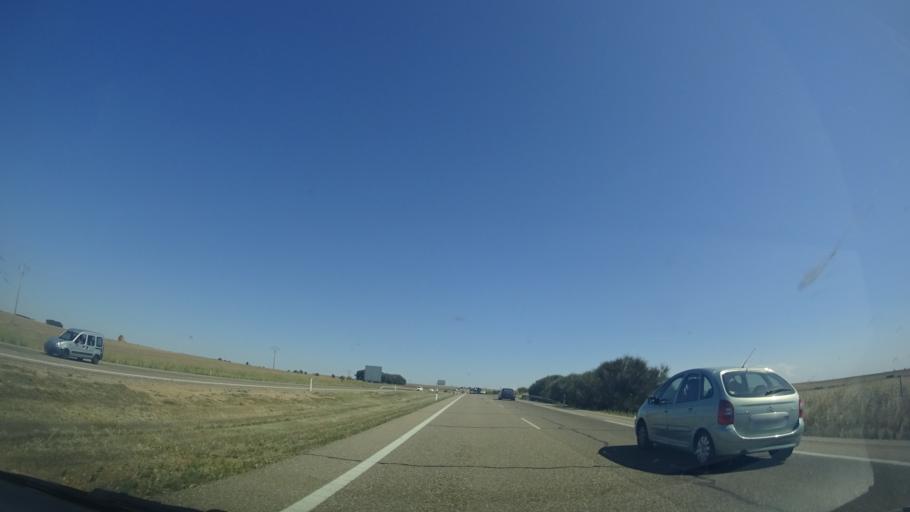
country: ES
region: Castille and Leon
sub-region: Provincia de Zamora
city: San Esteban del Molar
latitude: 41.9587
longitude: -5.5798
